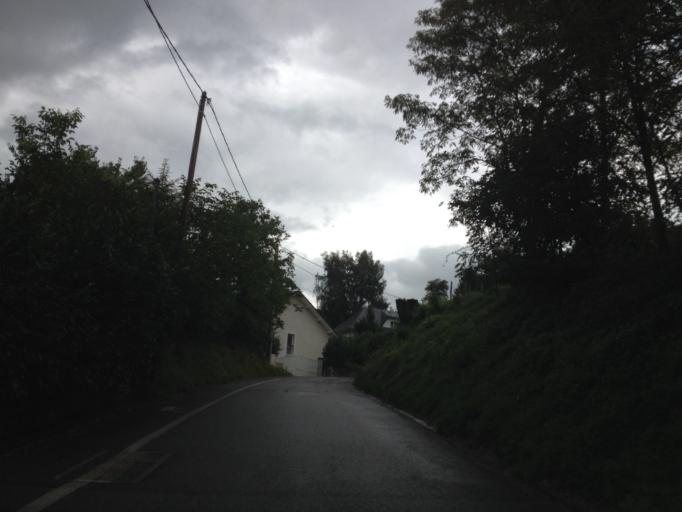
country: FR
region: Rhone-Alpes
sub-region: Departement de la Savoie
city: Sonnaz
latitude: 45.5984
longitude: 5.9054
